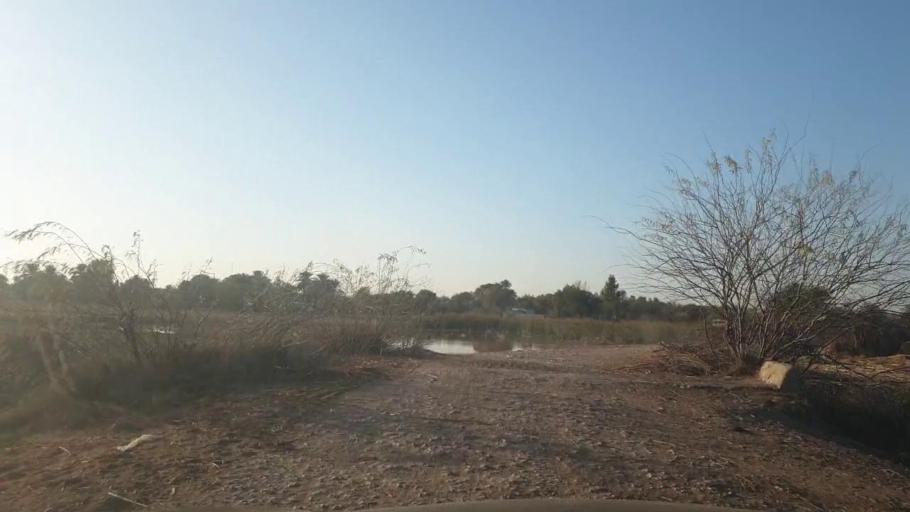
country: PK
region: Sindh
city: Mirpur Mathelo
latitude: 28.0030
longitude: 69.4669
